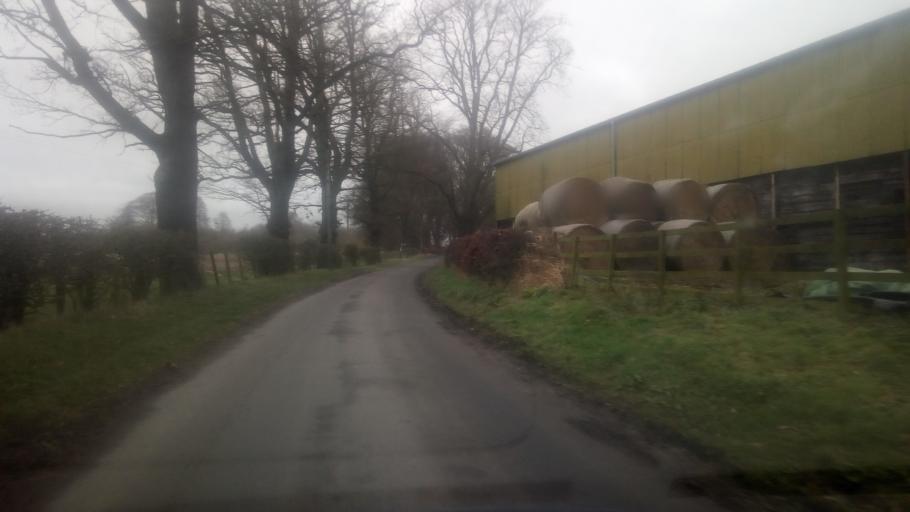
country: GB
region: Scotland
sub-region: The Scottish Borders
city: Jedburgh
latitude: 55.5276
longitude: -2.5148
